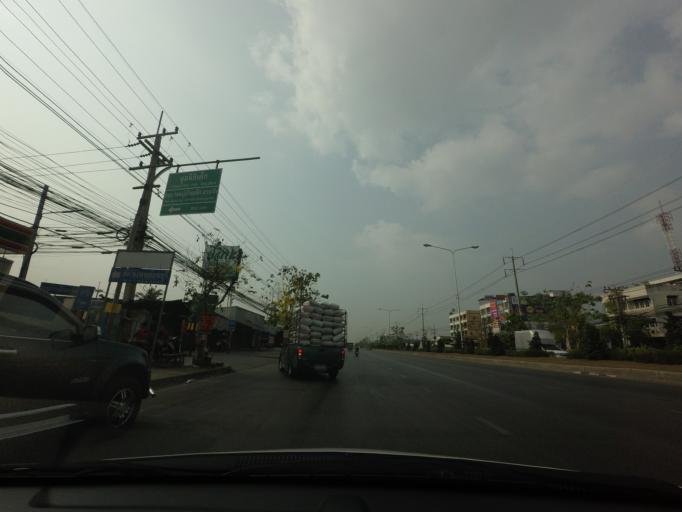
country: TH
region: Bangkok
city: Nong Khaem
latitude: 13.7393
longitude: 100.3295
